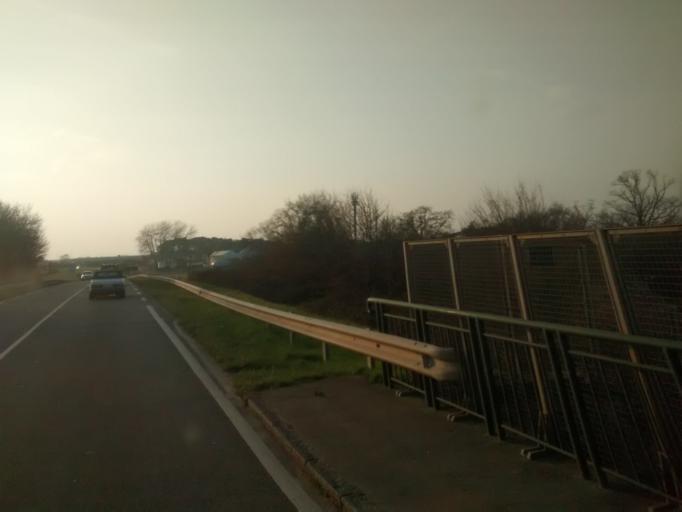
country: FR
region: Brittany
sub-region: Departement d'Ille-et-Vilaine
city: Saint-Jacques-de-la-Lande
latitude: 48.0539
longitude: -1.7281
